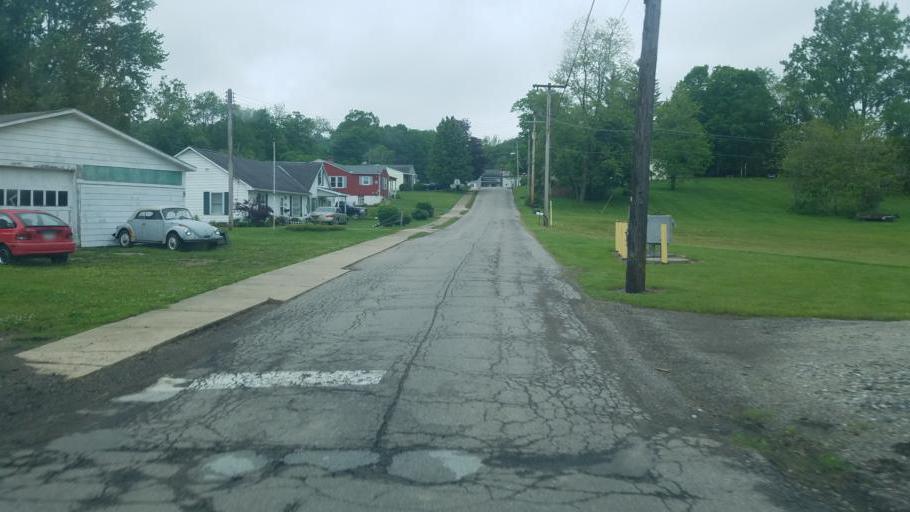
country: US
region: Ohio
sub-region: Richland County
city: Lincoln Heights
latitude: 40.7030
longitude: -82.4268
